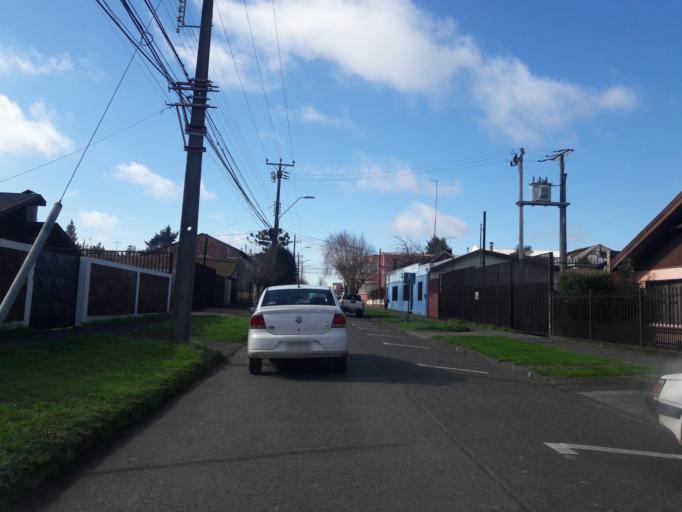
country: CL
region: Araucania
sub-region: Provincia de Malleco
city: Victoria
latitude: -38.2325
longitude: -72.3346
